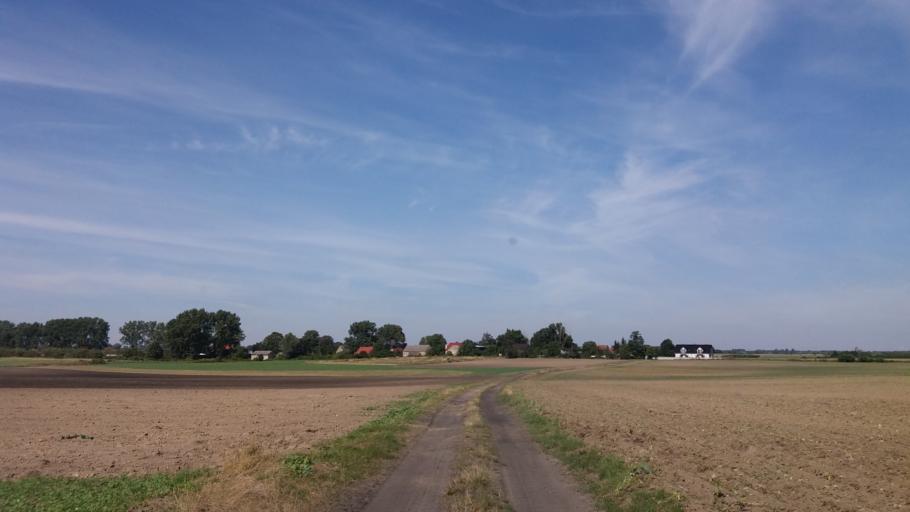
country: PL
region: West Pomeranian Voivodeship
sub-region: Powiat choszczenski
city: Choszczno
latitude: 53.1249
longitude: 15.4115
